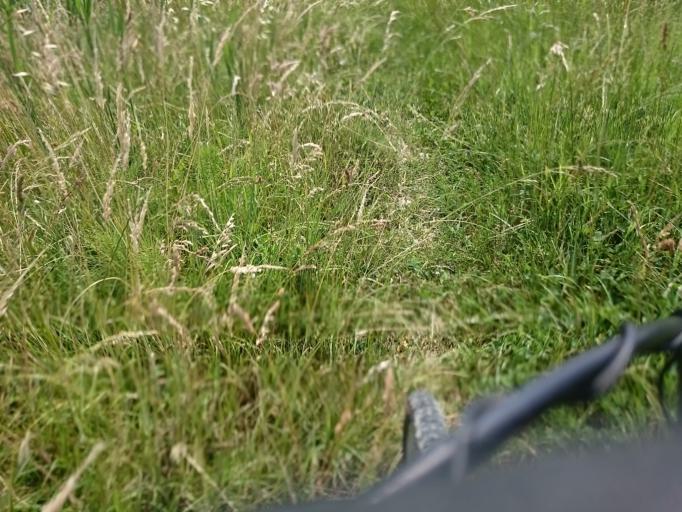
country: IT
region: Veneto
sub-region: Provincia di Padova
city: Codevigo
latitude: 45.2506
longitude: 12.1376
